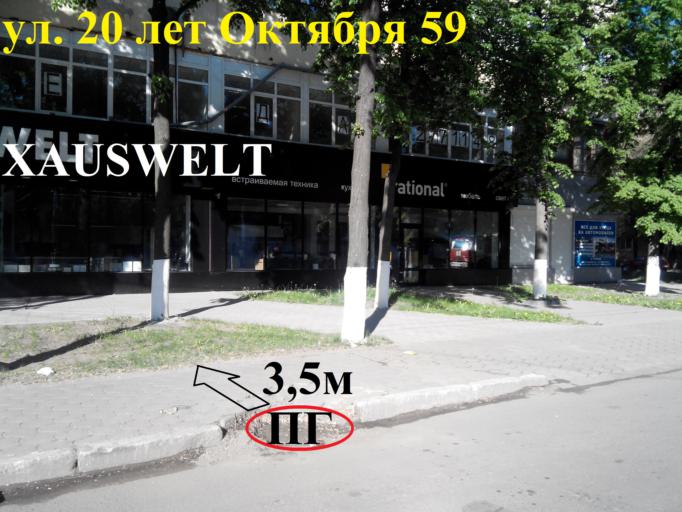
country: RU
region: Voronezj
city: Voronezh
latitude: 51.6455
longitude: 39.1986
